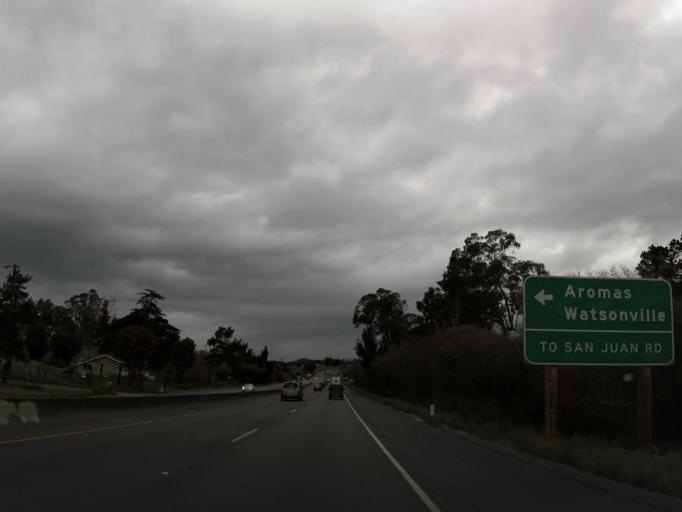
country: US
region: California
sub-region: San Benito County
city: Aromas
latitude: 36.8418
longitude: -121.6330
